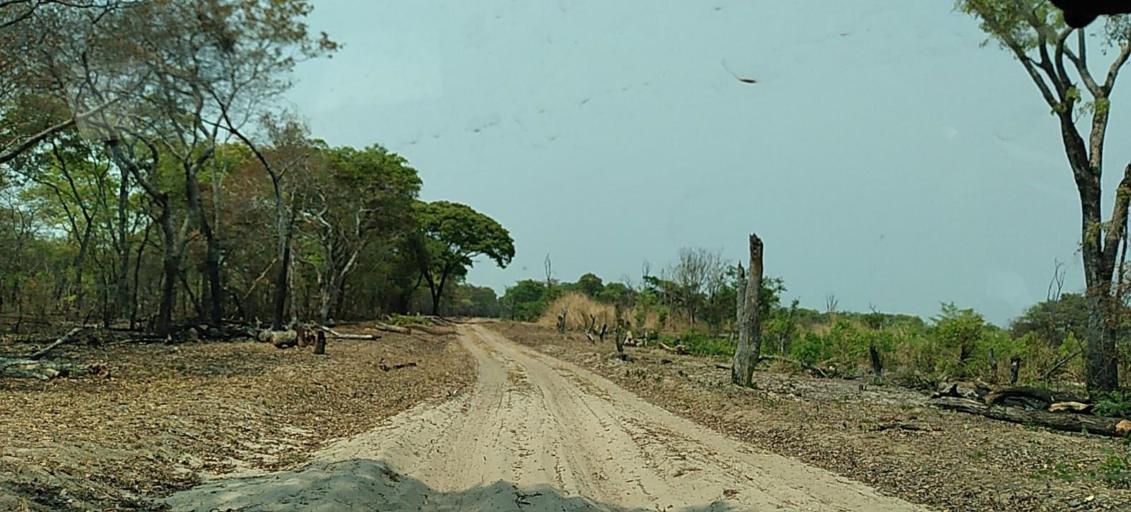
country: ZM
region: Western
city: Lukulu
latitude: -13.9539
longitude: 23.2245
